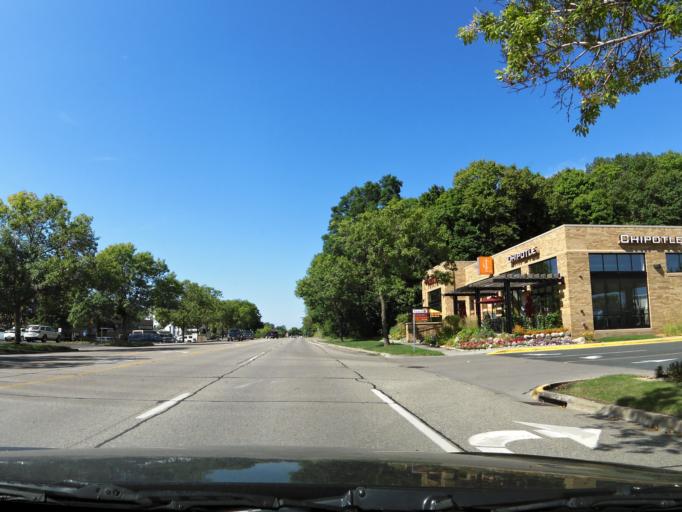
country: US
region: Minnesota
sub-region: Hennepin County
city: Wayzata
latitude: 44.9712
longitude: -93.4962
